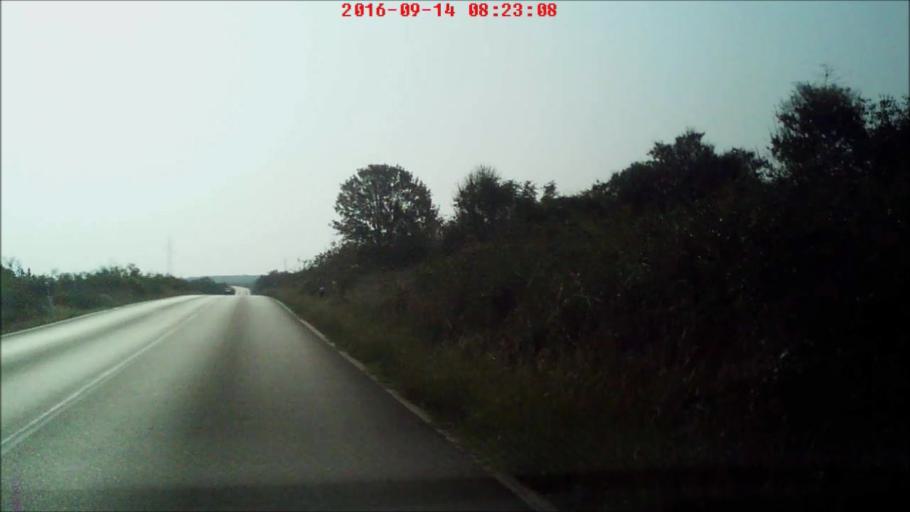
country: HR
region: Zadarska
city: Nin
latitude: 44.2143
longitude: 15.2271
